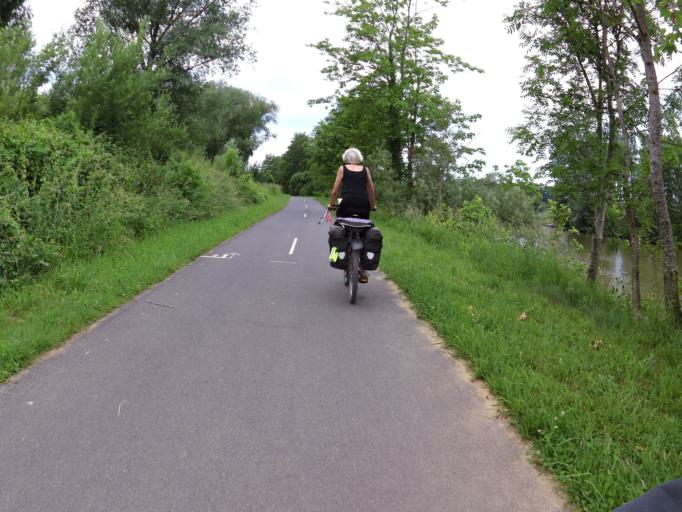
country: FR
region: Champagne-Ardenne
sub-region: Departement des Ardennes
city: Floing
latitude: 49.7130
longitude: 4.9185
